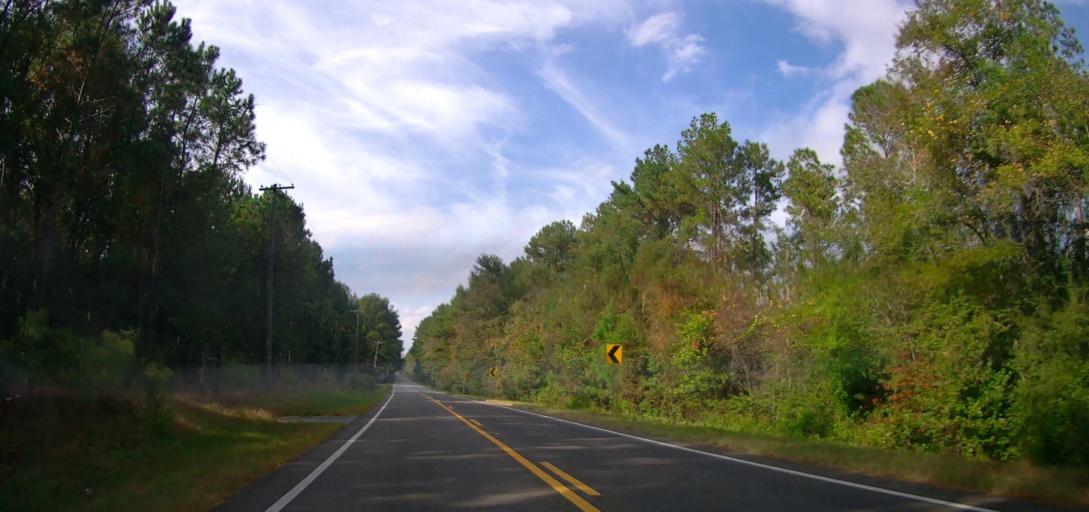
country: US
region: Georgia
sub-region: Thomas County
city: Thomasville
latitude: 30.9224
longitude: -84.0139
